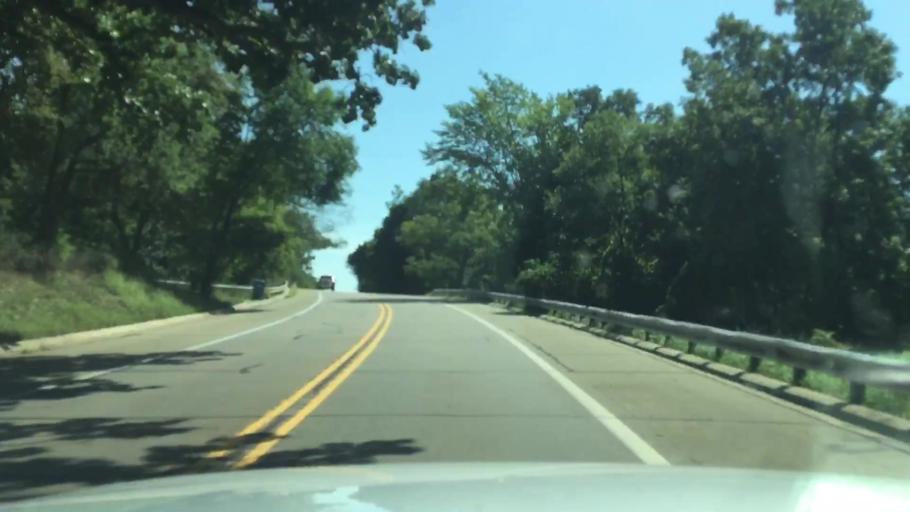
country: US
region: Michigan
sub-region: Jackson County
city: Brooklyn
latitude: 42.0599
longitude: -84.1808
